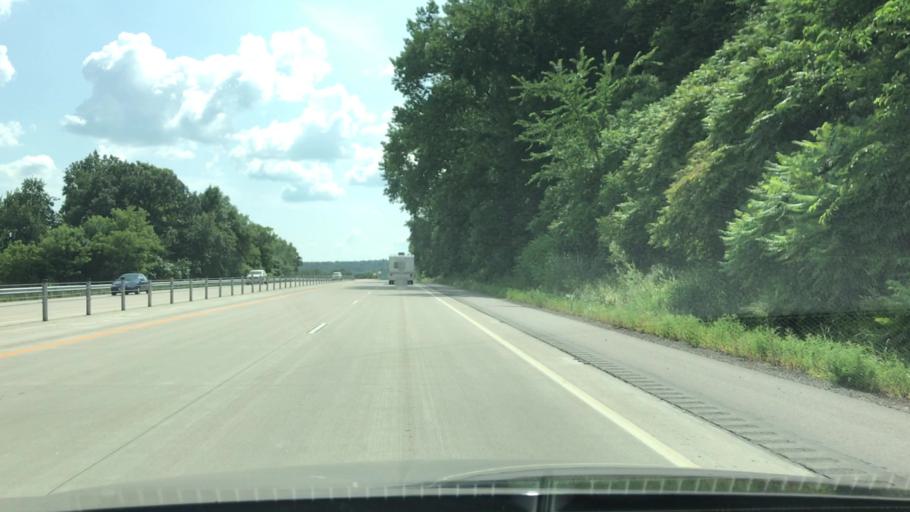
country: US
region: Minnesota
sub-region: Nicollet County
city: Saint Peter
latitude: 44.2774
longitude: -94.0134
